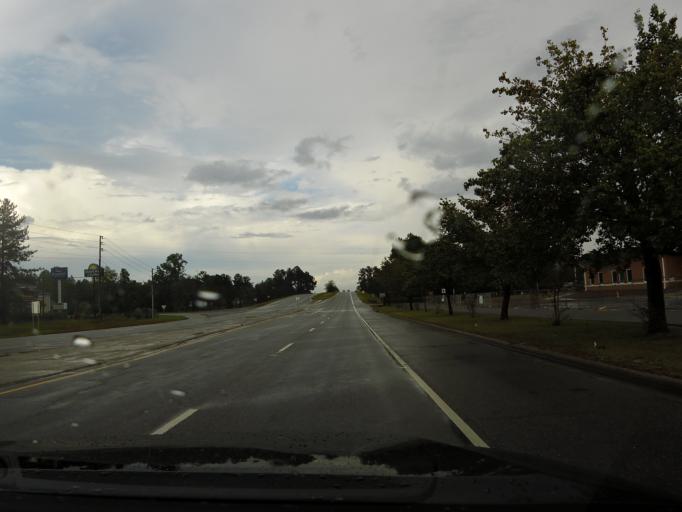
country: US
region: Georgia
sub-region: Wayne County
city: Jesup
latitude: 31.5955
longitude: -81.8694
